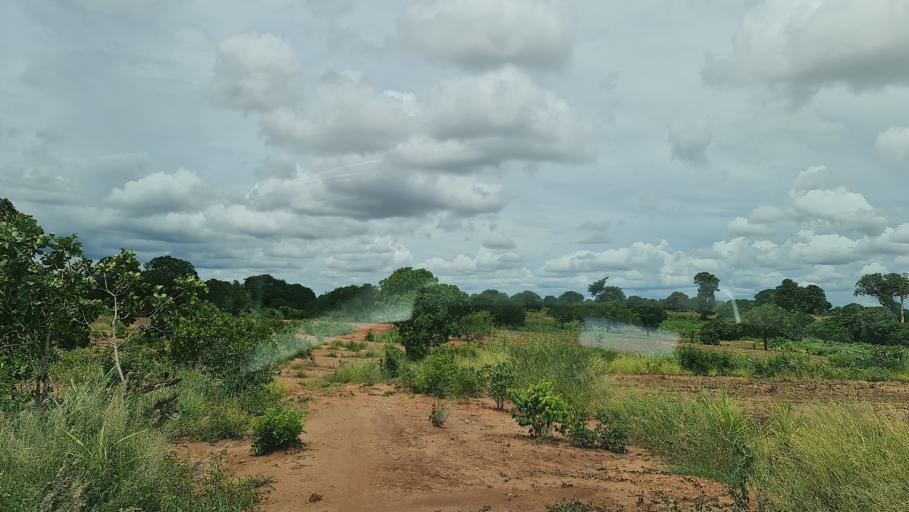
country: MZ
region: Nampula
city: Nacala
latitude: -14.7784
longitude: 39.9921
